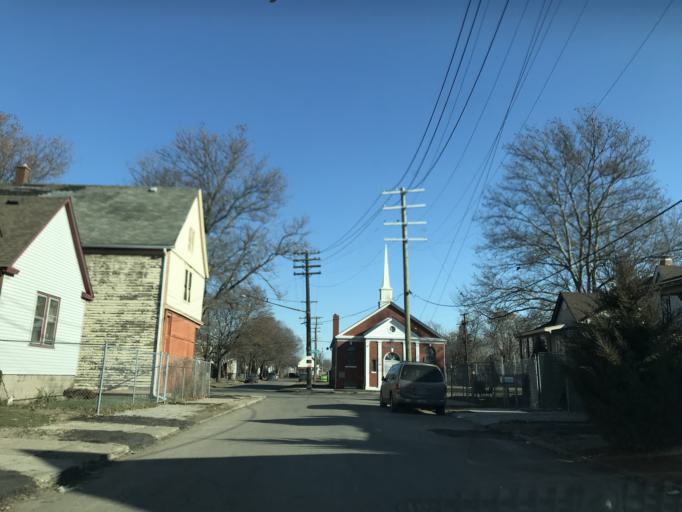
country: US
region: Michigan
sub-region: Wayne County
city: Dearborn
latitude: 42.3360
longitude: -83.1230
